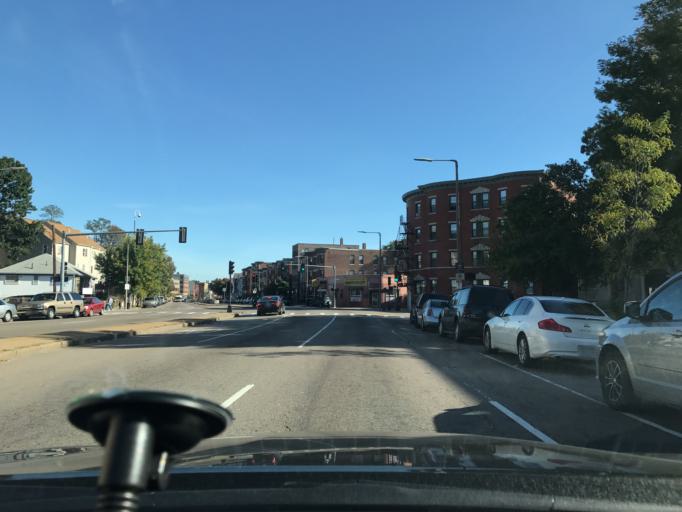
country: US
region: Massachusetts
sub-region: Suffolk County
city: South Boston
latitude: 42.3122
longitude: -71.0689
